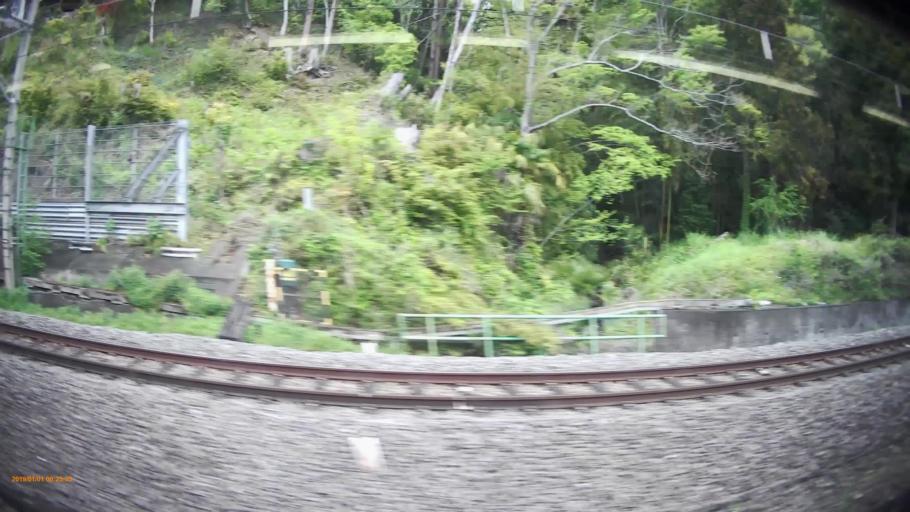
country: JP
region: Yamanashi
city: Uenohara
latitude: 35.6202
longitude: 139.1205
